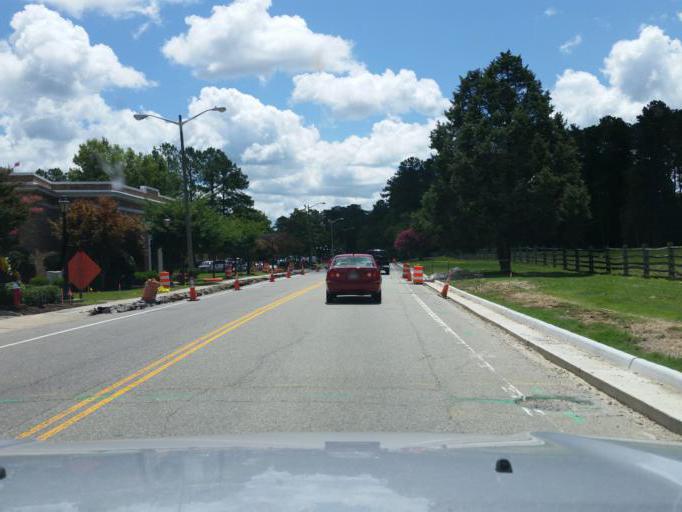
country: US
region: Virginia
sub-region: City of Williamsburg
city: Williamsburg
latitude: 37.2700
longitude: -76.6875
